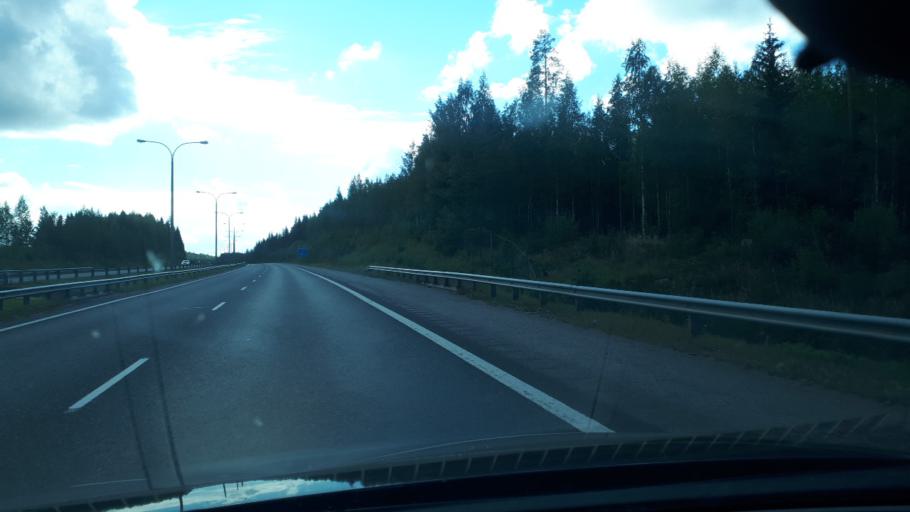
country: FI
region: Northern Savo
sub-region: Kuopio
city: Siilinjaervi
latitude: 63.0297
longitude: 27.6566
